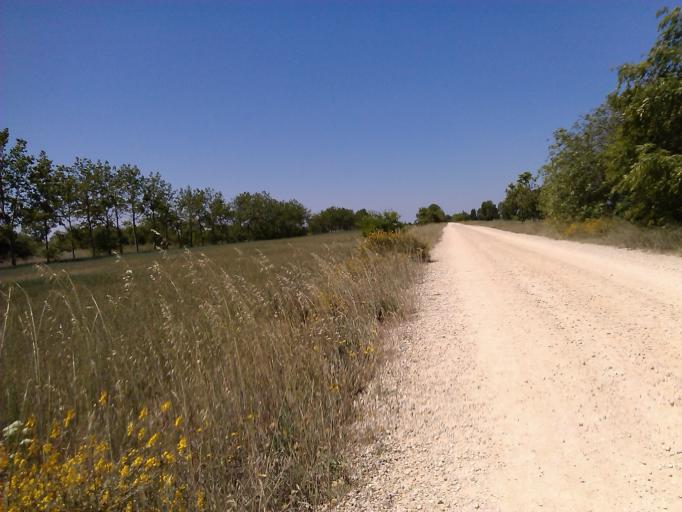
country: ES
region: Castille and Leon
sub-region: Provincia de Palencia
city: Calzada de los Molinos
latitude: 42.3438
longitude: -4.6719
